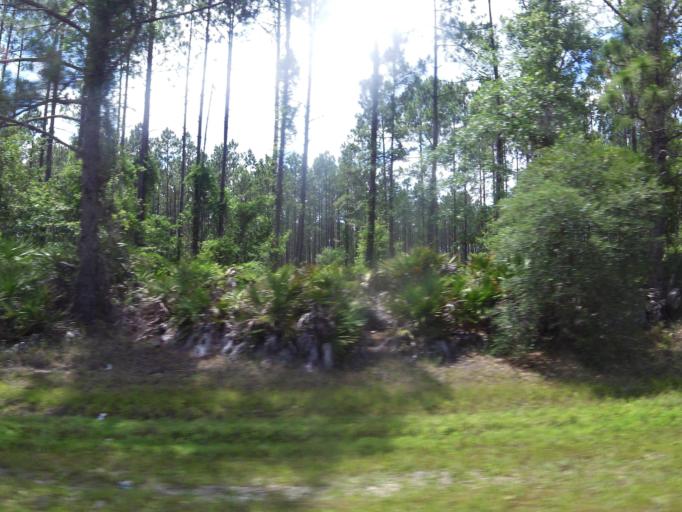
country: US
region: Florida
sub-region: Clay County
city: Green Cove Springs
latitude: 29.9299
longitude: -81.7540
